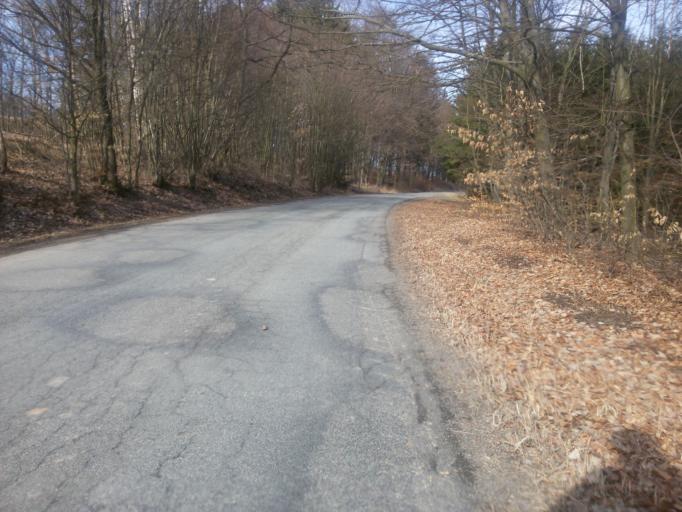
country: CZ
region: South Moravian
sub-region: Okres Brno-Venkov
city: Lomnice
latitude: 49.4255
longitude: 16.4090
